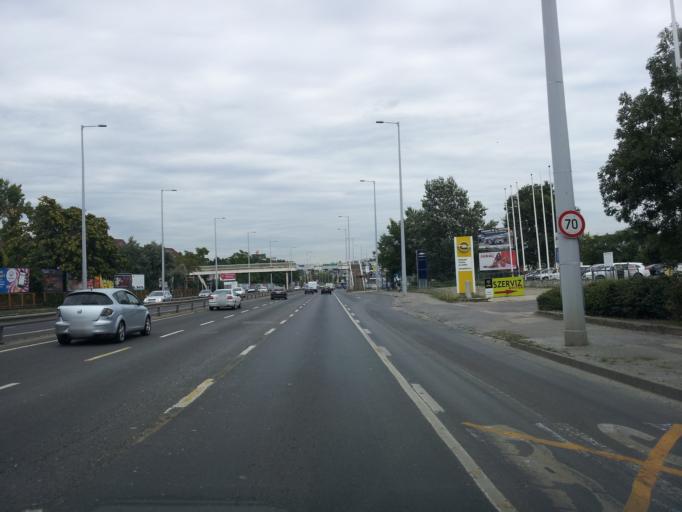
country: HU
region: Budapest
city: Budapest XI. keruelet
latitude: 47.4698
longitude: 19.0194
